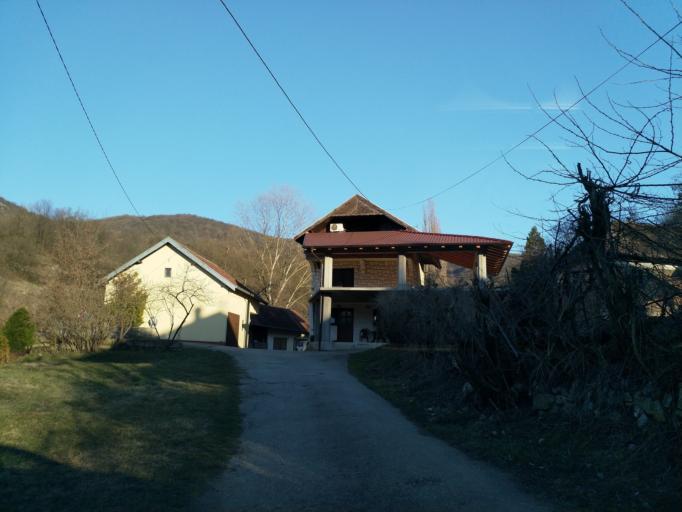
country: RS
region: Central Serbia
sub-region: Pomoravski Okrug
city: Paracin
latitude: 43.9297
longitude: 21.5213
